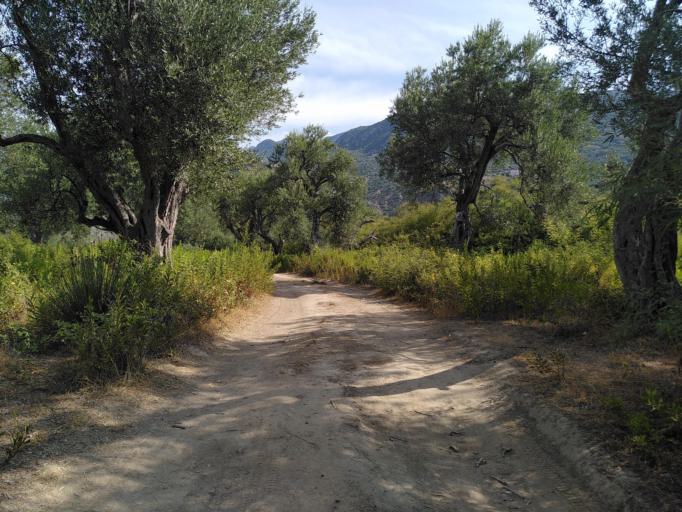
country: AL
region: Vlore
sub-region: Rrethi i Vlores
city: Himare
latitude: 40.0539
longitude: 19.8193
